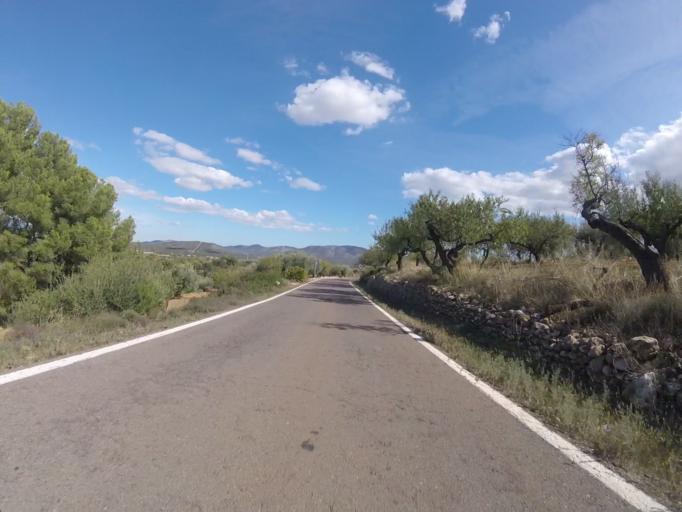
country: ES
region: Valencia
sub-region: Provincia de Castello
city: Cuevas de Vinroma
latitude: 40.3804
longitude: 0.1045
